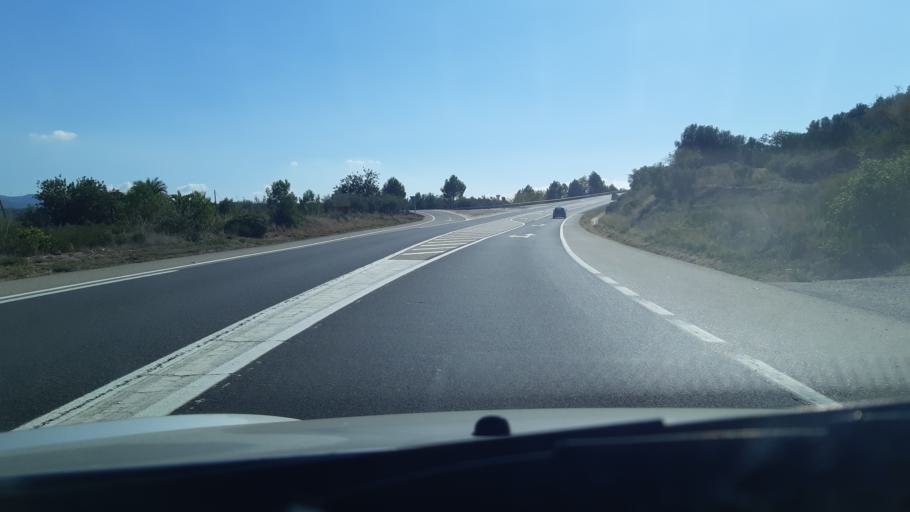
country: ES
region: Catalonia
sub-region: Provincia de Tarragona
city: Tivenys
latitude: 40.9180
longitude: 0.4939
